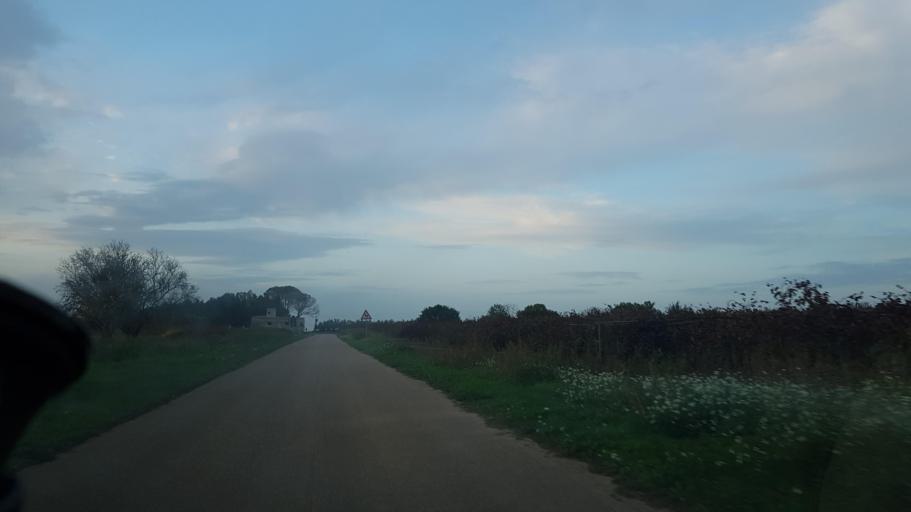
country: IT
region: Apulia
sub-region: Provincia di Brindisi
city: San Donaci
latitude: 40.4309
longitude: 17.9302
